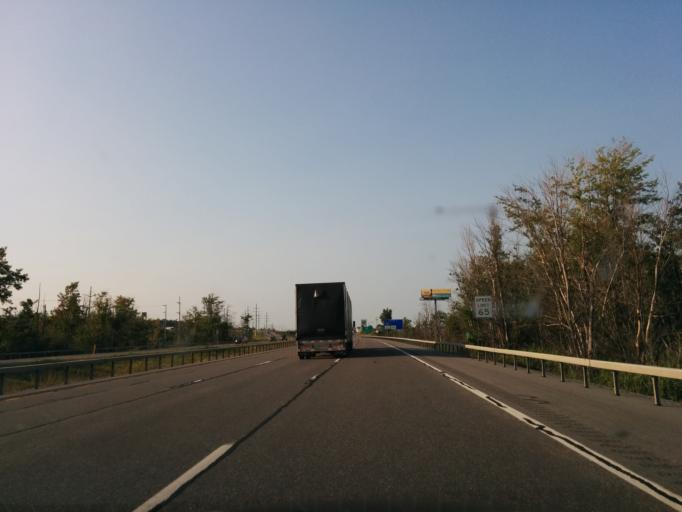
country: US
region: New York
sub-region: Jefferson County
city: Watertown
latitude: 43.9682
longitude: -75.9489
